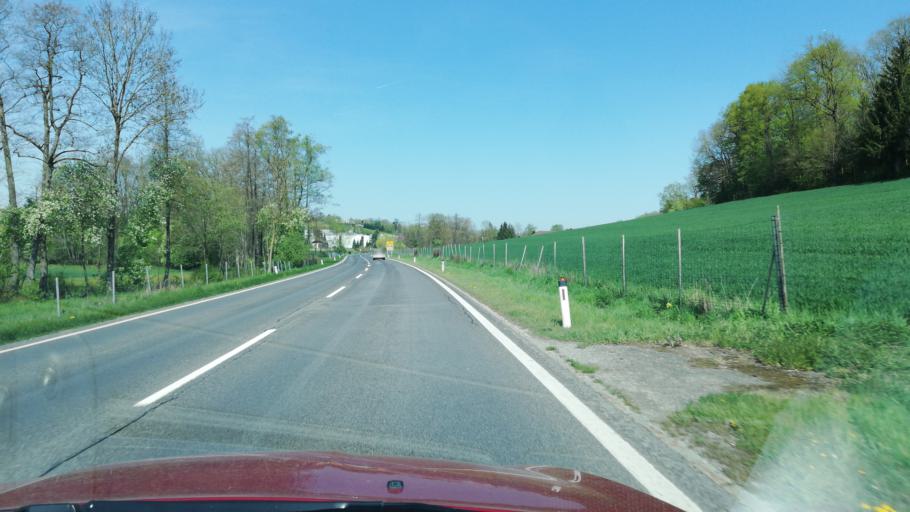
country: AT
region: Upper Austria
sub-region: Wels-Land
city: Thalheim bei Wels
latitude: 48.1327
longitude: 14.0506
